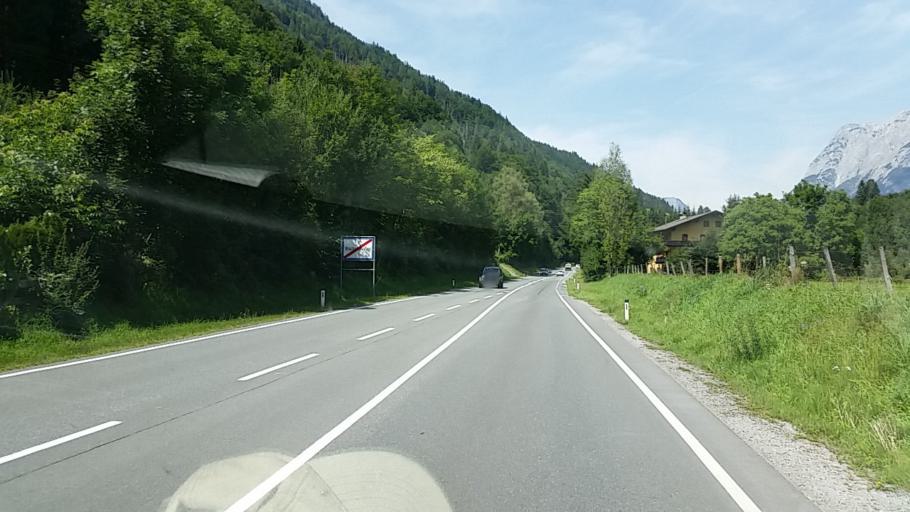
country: AT
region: Salzburg
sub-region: Politischer Bezirk Sankt Johann im Pongau
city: Bischofshofen
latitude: 47.4305
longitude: 13.2124
